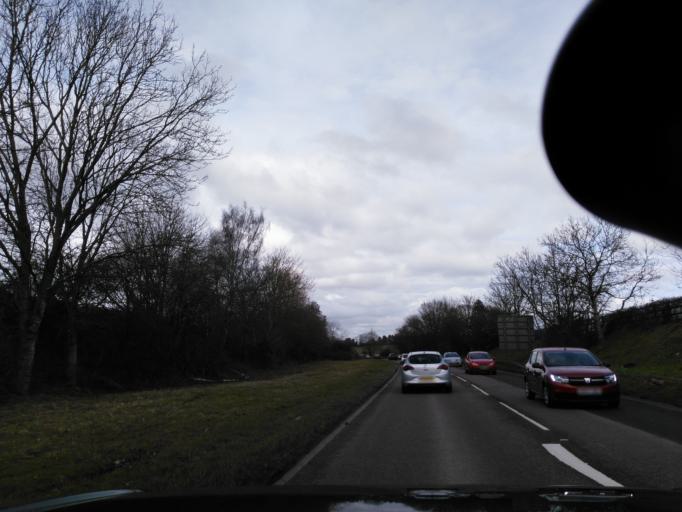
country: GB
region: England
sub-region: Wiltshire
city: Lacock
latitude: 51.4222
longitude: -2.1267
